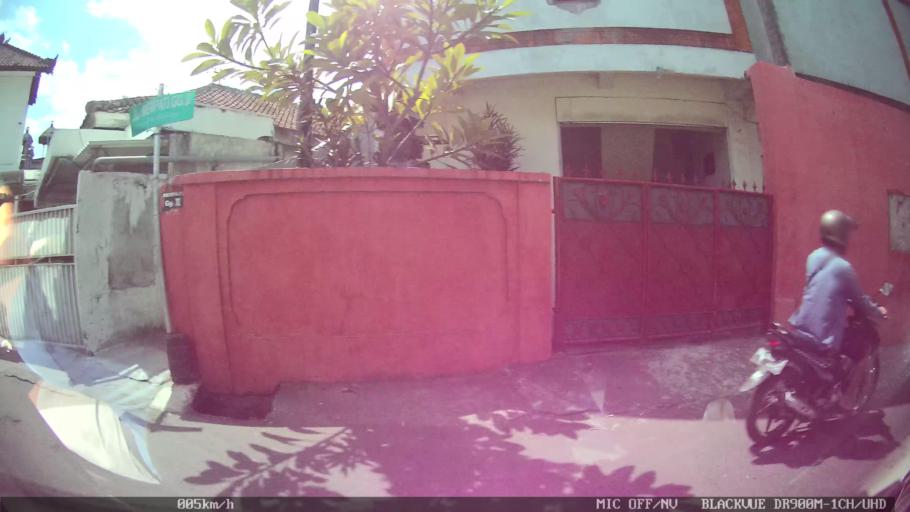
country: ID
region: Bali
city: Denpasar
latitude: -8.6597
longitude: 115.1976
